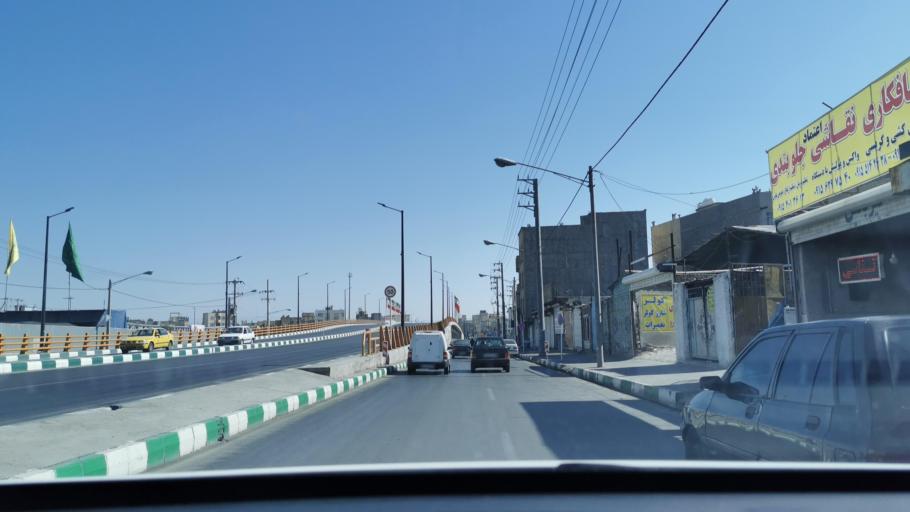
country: IR
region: Razavi Khorasan
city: Mashhad
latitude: 36.3348
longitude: 59.6039
